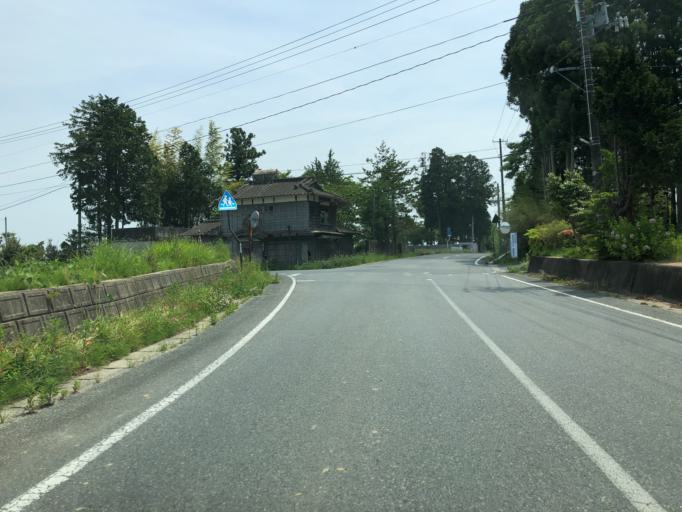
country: JP
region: Fukushima
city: Namie
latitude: 37.5192
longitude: 140.9326
